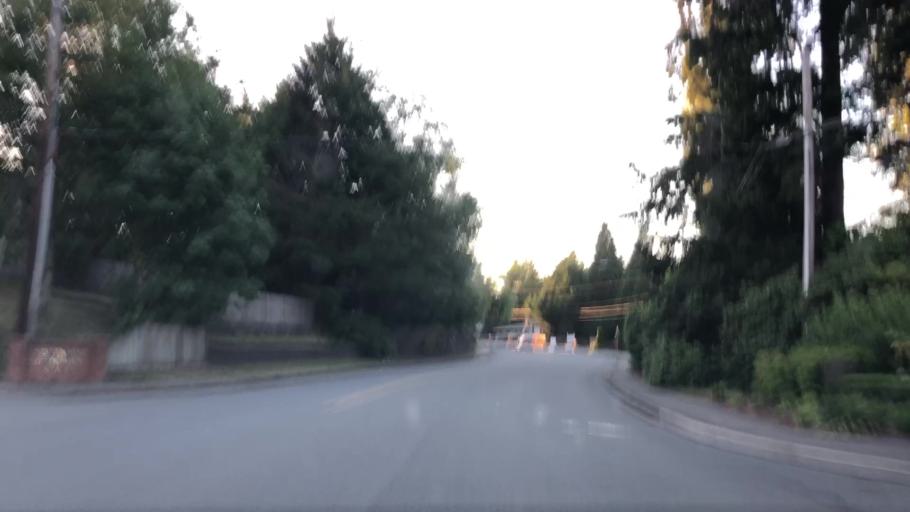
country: US
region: Washington
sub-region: Snohomish County
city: Brier
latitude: 47.7776
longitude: -122.2716
